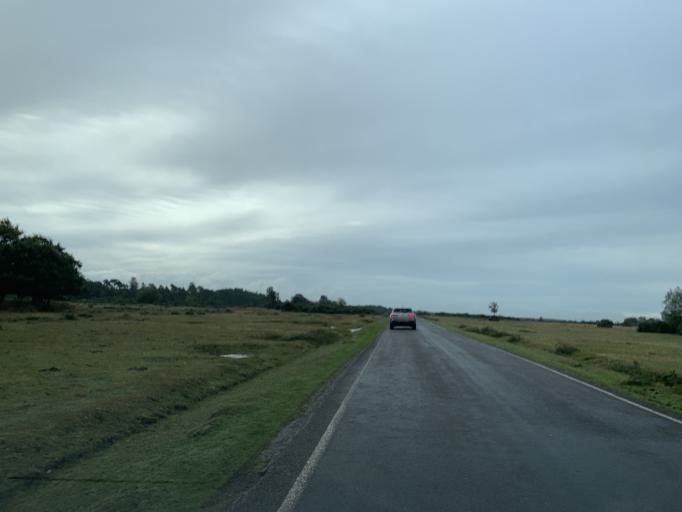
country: GB
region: England
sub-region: Hampshire
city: Cadnam
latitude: 50.9238
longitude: -1.6532
